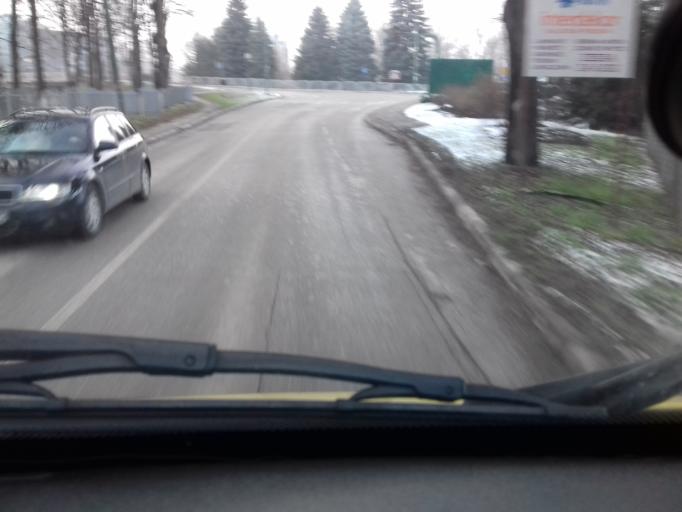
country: BA
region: Federation of Bosnia and Herzegovina
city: Visoko
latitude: 43.9900
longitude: 18.1849
